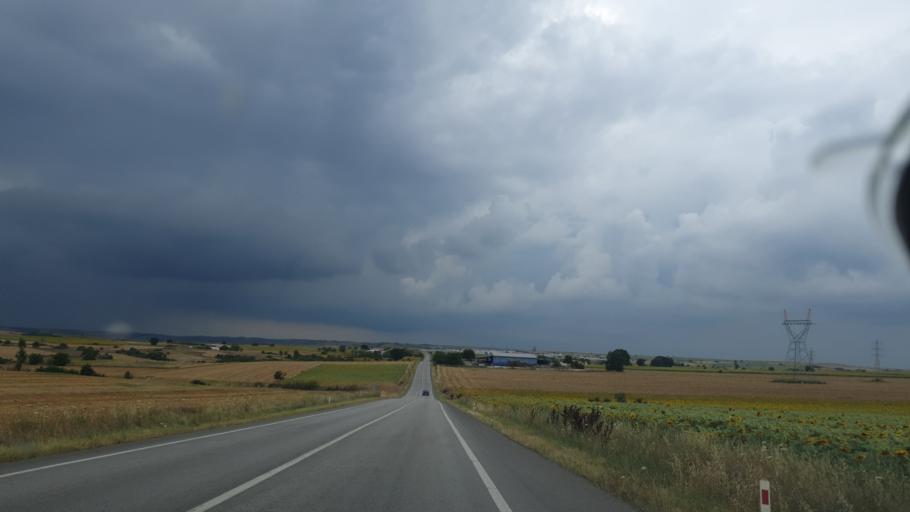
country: TR
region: Tekirdag
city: Hayrabolu
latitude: 41.2183
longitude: 27.0841
